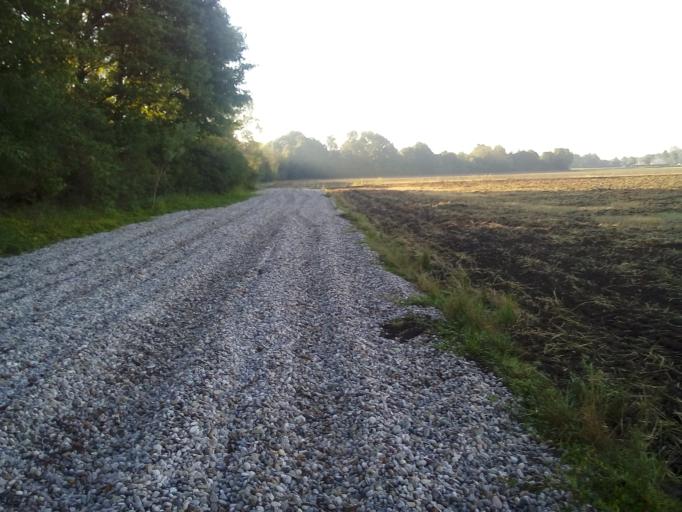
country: DE
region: Bavaria
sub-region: Upper Bavaria
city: Aschheim
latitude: 48.1600
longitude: 11.6882
